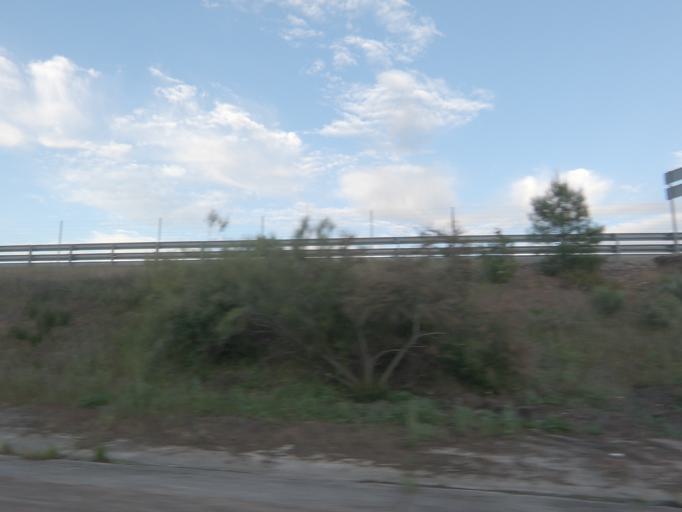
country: ES
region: Extremadura
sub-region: Provincia de Badajoz
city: Aljucen
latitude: 39.0717
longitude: -6.3131
